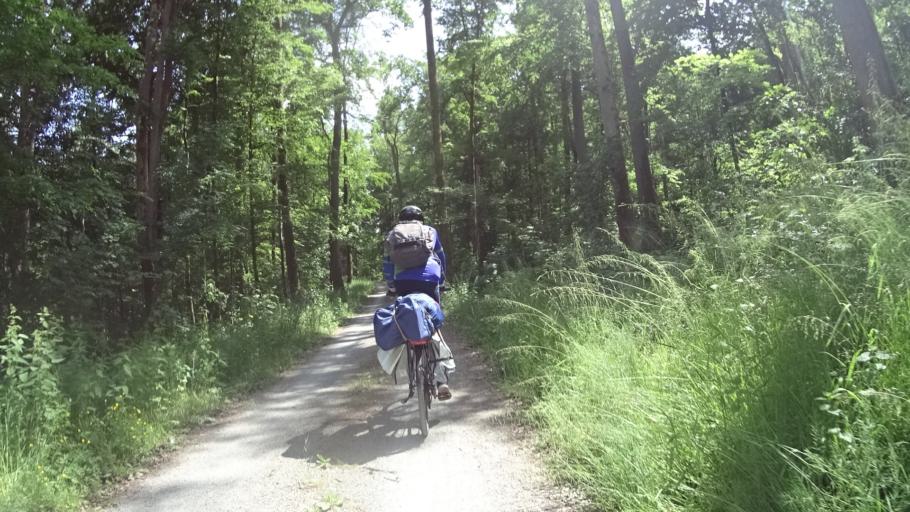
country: DE
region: Bavaria
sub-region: Regierungsbezirk Unterfranken
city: Neunkirchen
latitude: 49.6579
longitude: 9.4270
